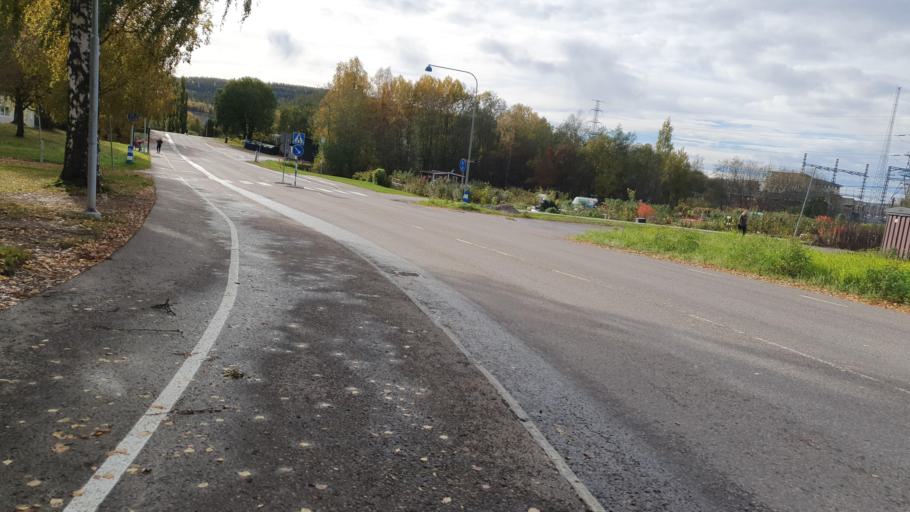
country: SE
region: Vaesternorrland
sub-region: Sundsvalls Kommun
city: Sundsvall
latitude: 62.4069
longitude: 17.2457
